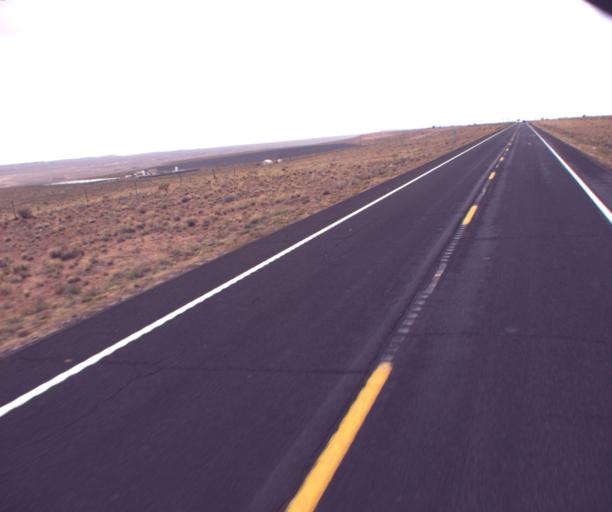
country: US
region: Arizona
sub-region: Coconino County
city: Tuba City
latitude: 36.1538
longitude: -111.1250
